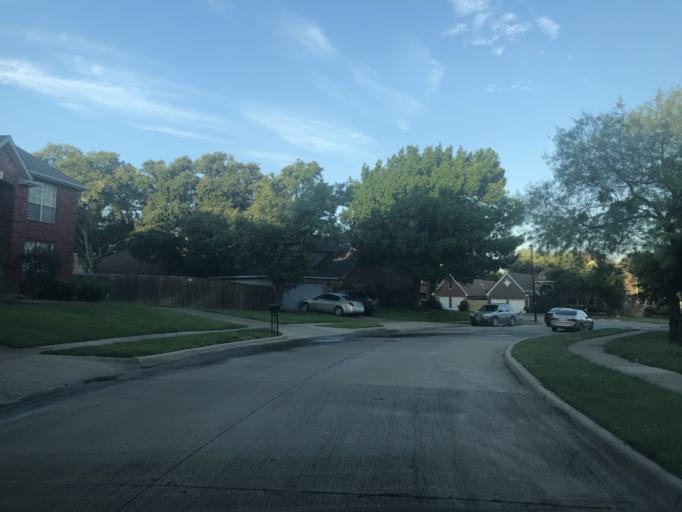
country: US
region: Texas
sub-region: Dallas County
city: Duncanville
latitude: 32.6490
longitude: -96.9690
